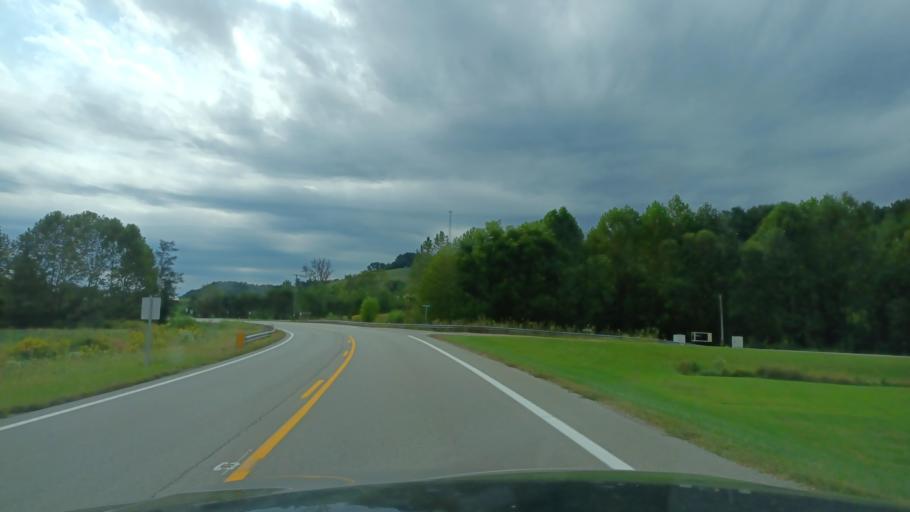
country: US
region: Ohio
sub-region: Vinton County
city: McArthur
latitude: 39.2689
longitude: -82.6775
